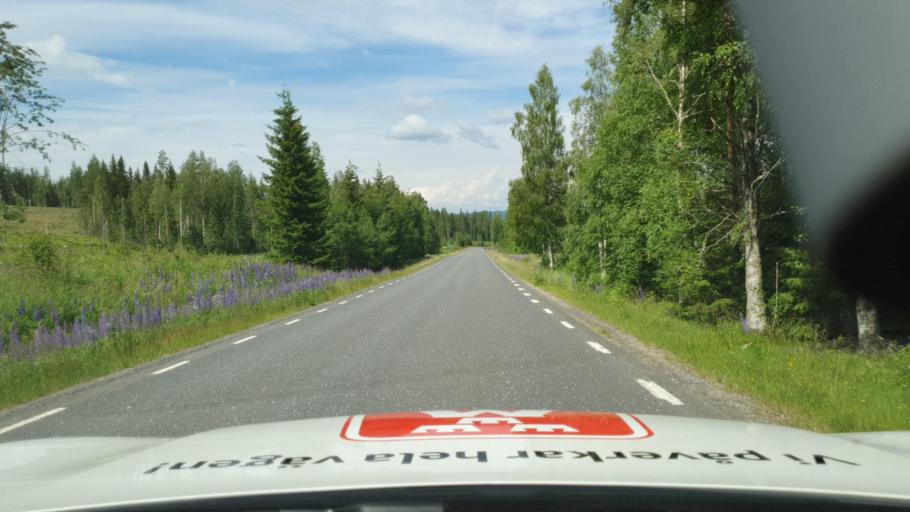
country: SE
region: Vaermland
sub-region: Torsby Kommun
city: Torsby
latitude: 60.6591
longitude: 12.7024
